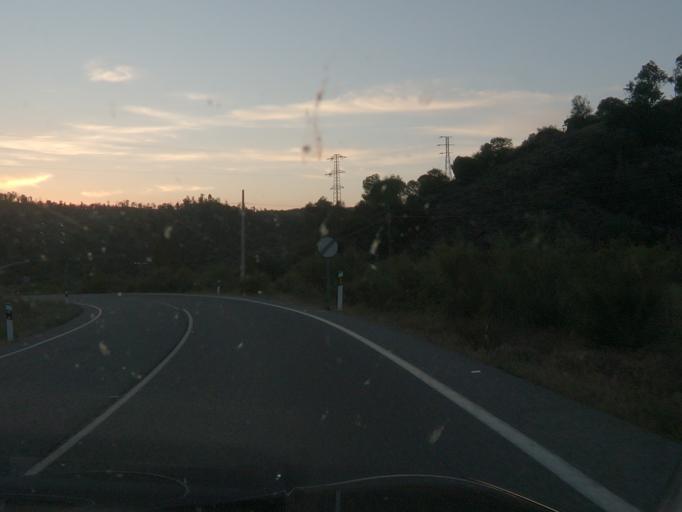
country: ES
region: Extremadura
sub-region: Provincia de Caceres
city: Alcantara
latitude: 39.7226
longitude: -6.8837
